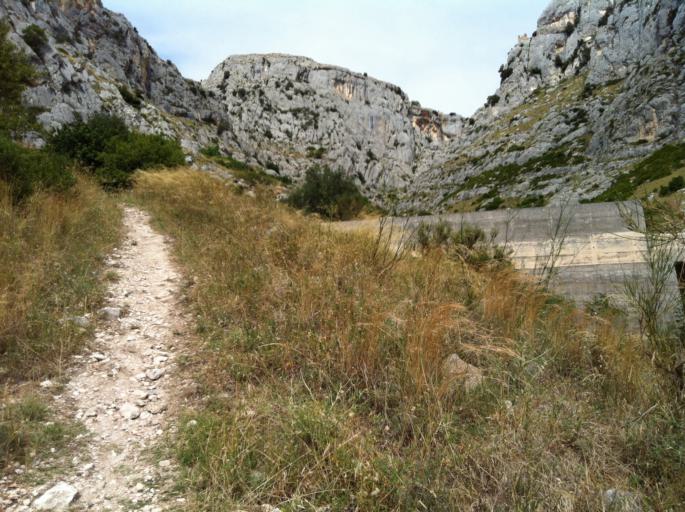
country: IT
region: Apulia
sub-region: Provincia di Foggia
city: Manfredonia
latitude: 41.6717
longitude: 15.9089
